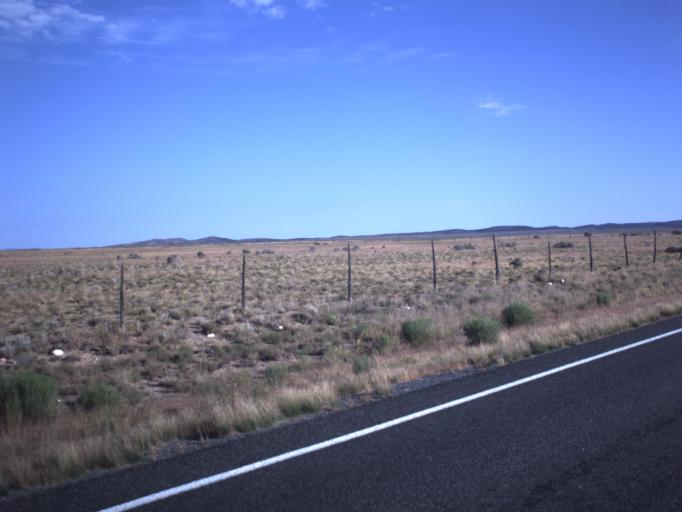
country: US
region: Utah
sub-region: Iron County
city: Enoch
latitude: 37.9015
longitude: -113.0315
